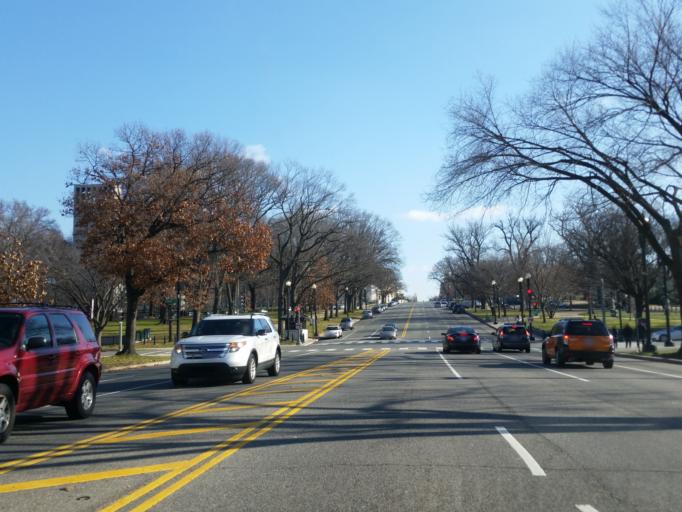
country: US
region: Washington, D.C.
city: Washington, D.C.
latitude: 38.8921
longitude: -77.0129
